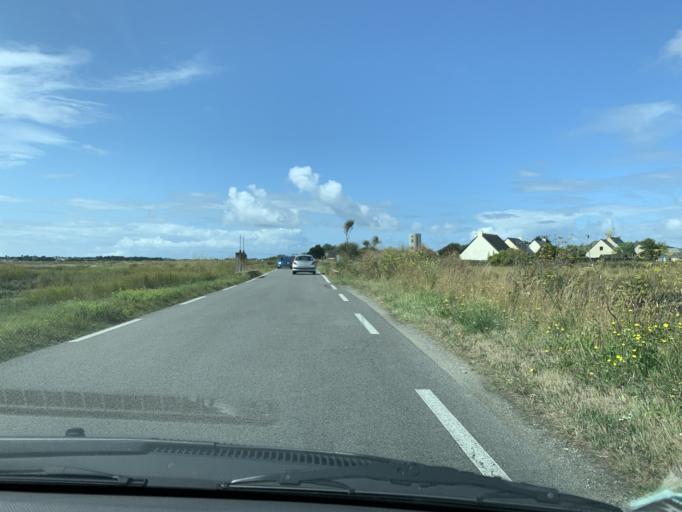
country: FR
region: Pays de la Loire
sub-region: Departement de la Loire-Atlantique
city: Le Pouliguen
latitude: 47.2972
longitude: -2.4214
